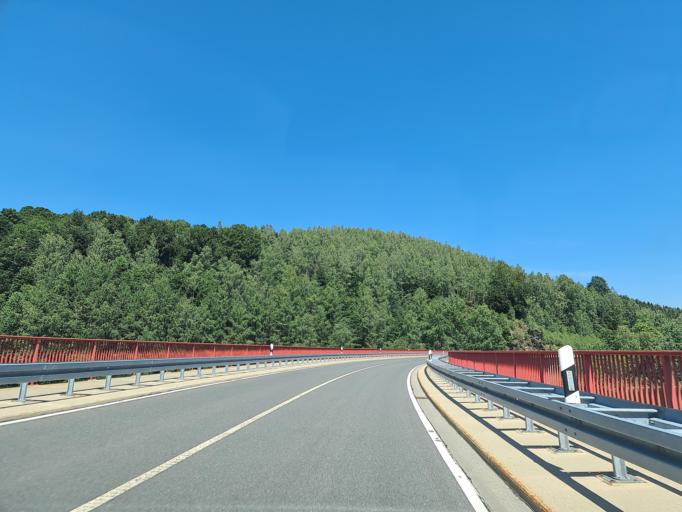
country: DE
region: Saxony
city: Rechenberg-Bienenmuhle
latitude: 50.7047
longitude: 13.5239
